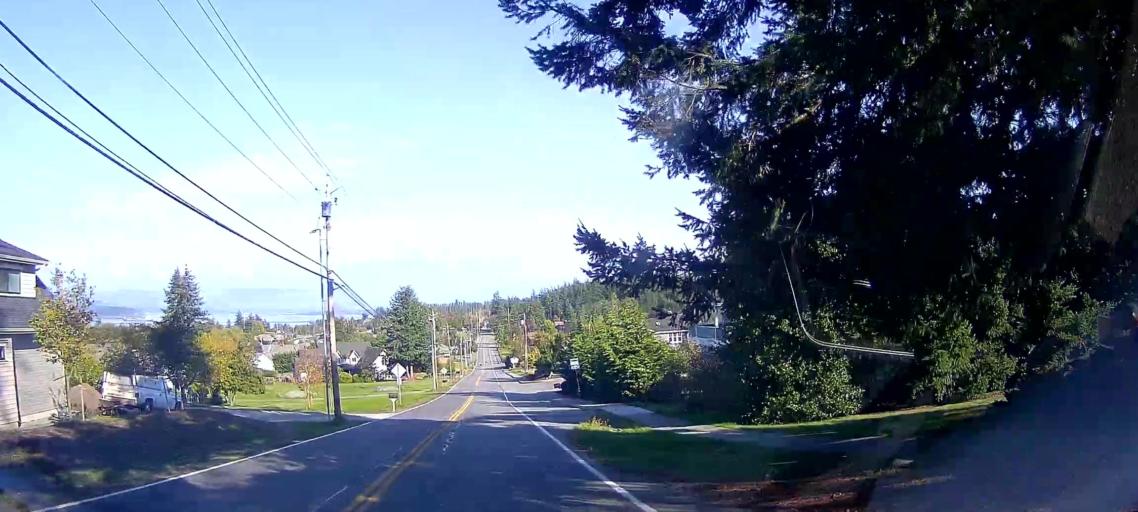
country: US
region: Washington
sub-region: Skagit County
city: Anacortes
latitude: 48.4879
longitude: -122.6306
